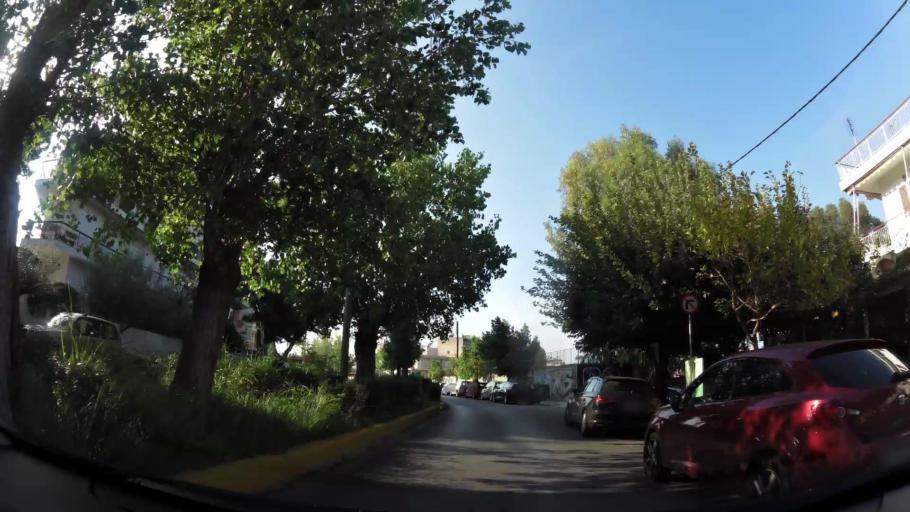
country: GR
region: Attica
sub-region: Nomarchia Athinas
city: Agios Dimitrios
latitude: 37.9310
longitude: 23.7474
